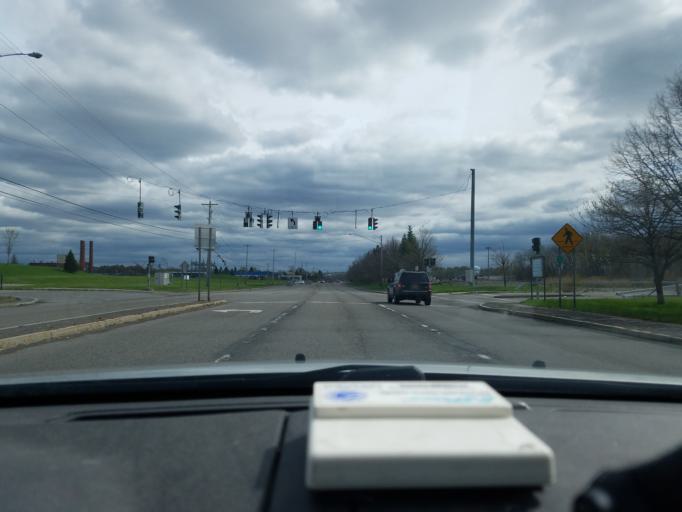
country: US
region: New York
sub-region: Onondaga County
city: East Syracuse
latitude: 43.0853
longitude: -76.0901
